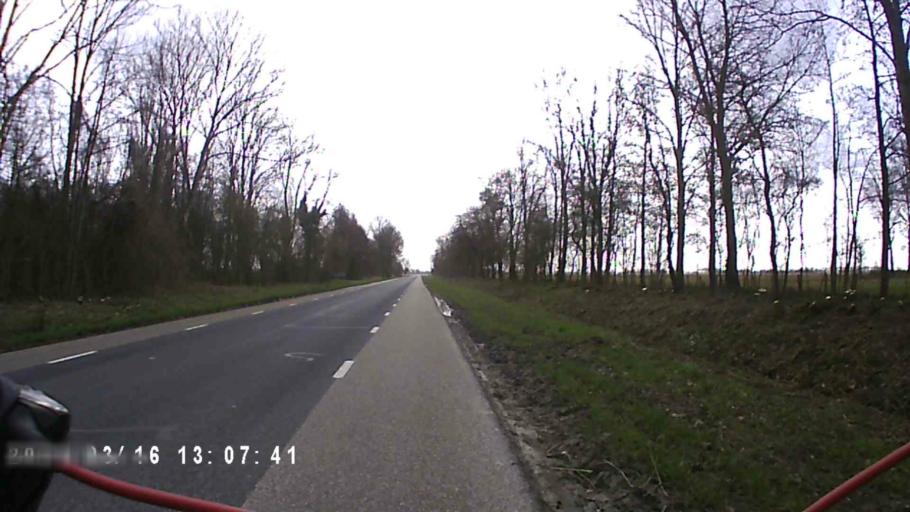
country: NL
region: Friesland
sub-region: Gemeente Het Bildt
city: Minnertsga
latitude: 53.2505
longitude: 5.6202
